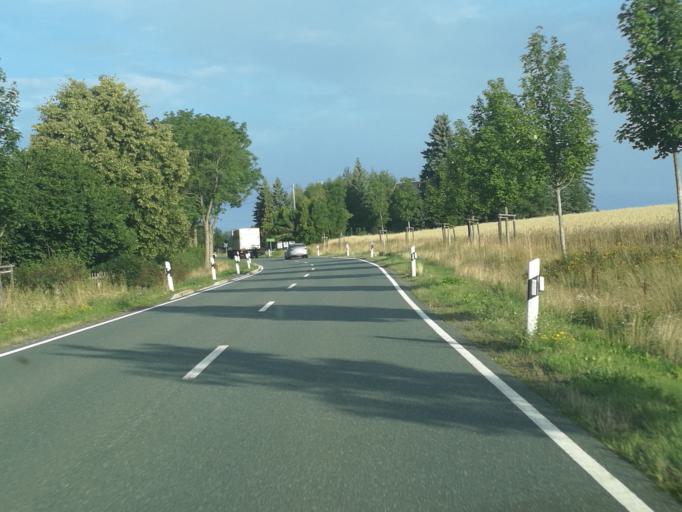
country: DE
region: Saxony
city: Adorf
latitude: 50.3333
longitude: 12.2269
